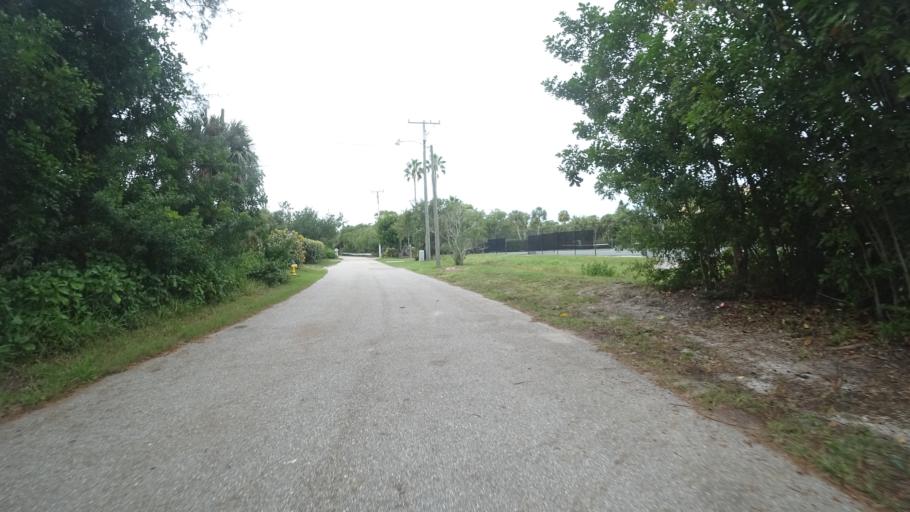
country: US
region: Florida
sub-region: Manatee County
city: Longboat Key
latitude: 27.4231
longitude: -82.6672
